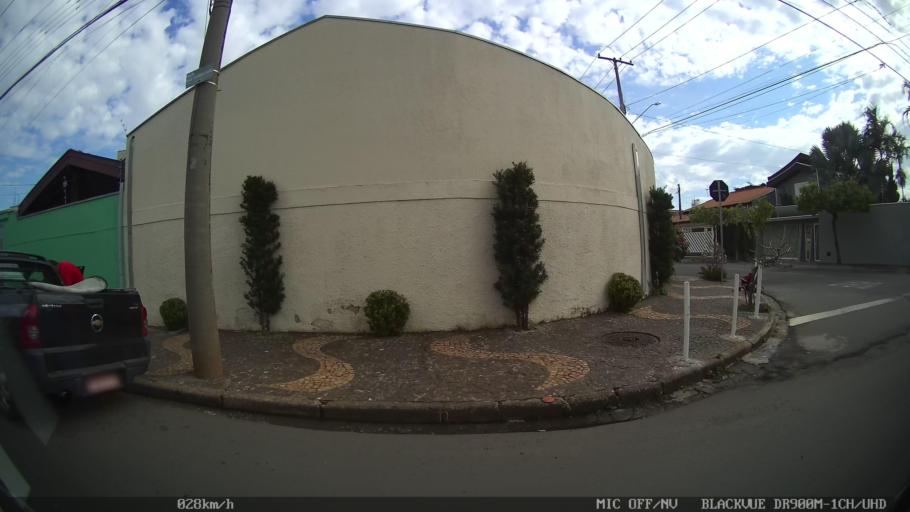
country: BR
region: Sao Paulo
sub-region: Americana
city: Americana
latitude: -22.7421
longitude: -47.3558
